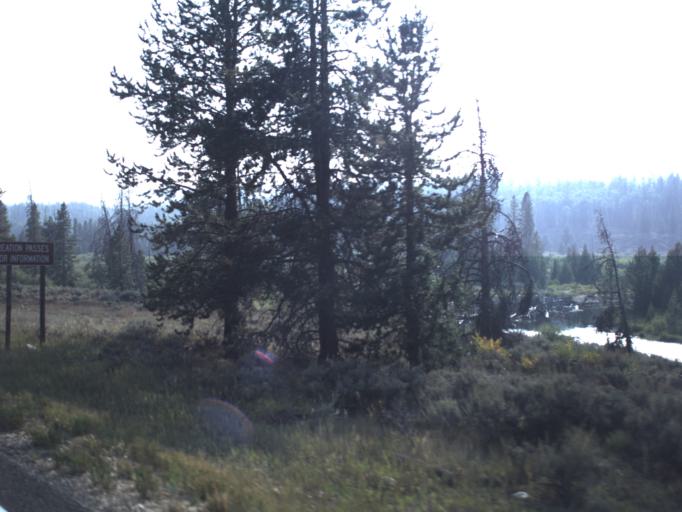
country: US
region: Wyoming
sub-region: Uinta County
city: Evanston
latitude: 40.8864
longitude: -110.8319
